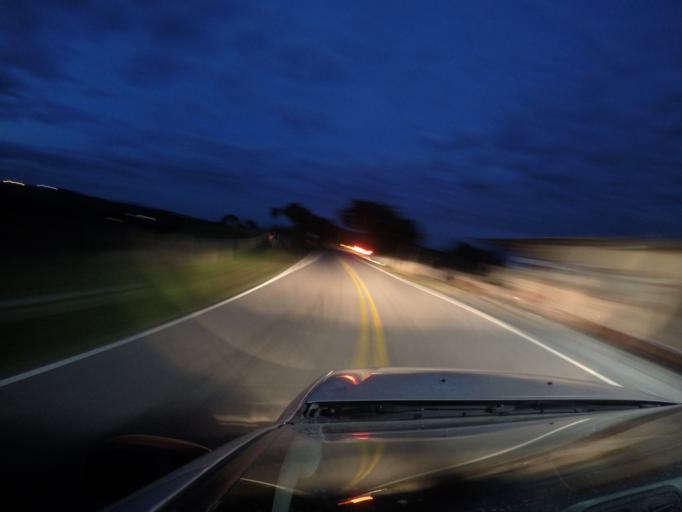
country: CO
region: Tolima
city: Fresno
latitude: 5.1569
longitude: -75.0669
